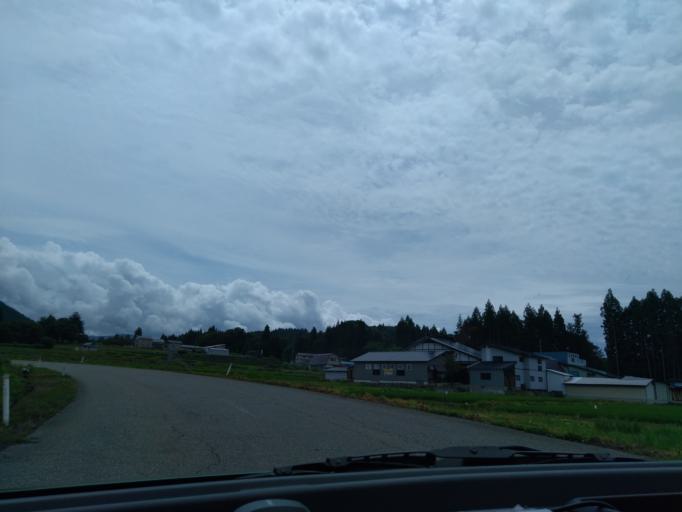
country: JP
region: Akita
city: Kakunodatemachi
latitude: 39.5822
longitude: 140.6229
